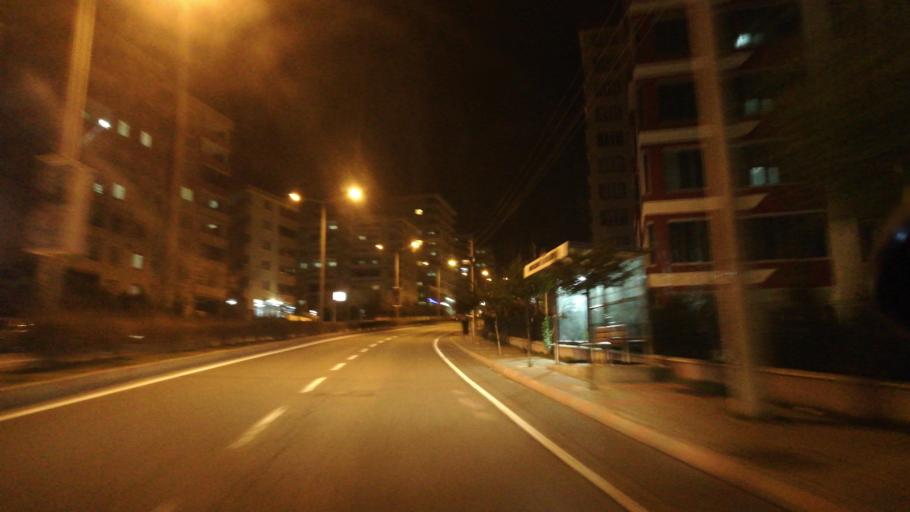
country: TR
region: Kahramanmaras
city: Kahramanmaras
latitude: 37.5890
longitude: 36.8579
